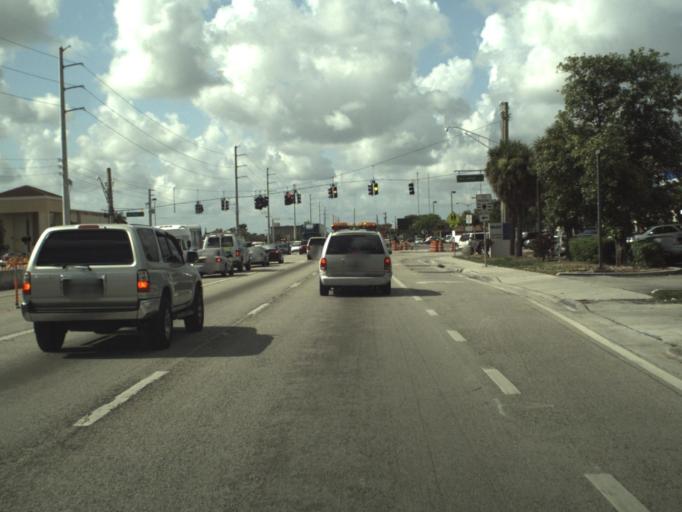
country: US
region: Florida
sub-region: Broward County
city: Pembroke Pines
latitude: 26.0110
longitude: -80.2077
